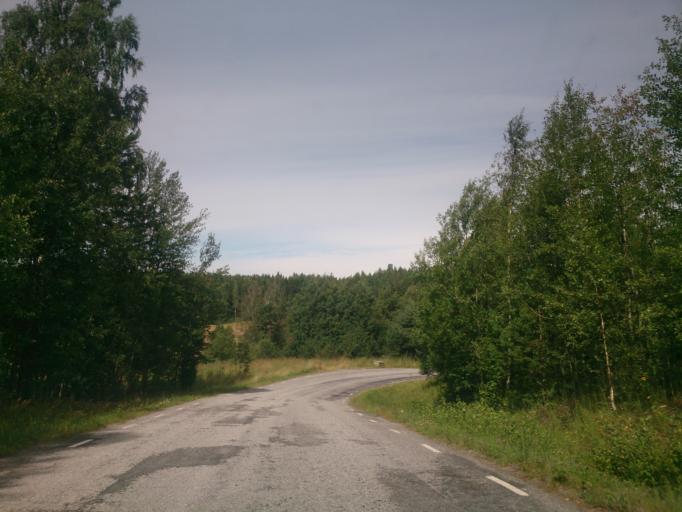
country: SE
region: OEstergoetland
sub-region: Valdemarsviks Kommun
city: Gusum
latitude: 58.3347
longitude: 16.5839
